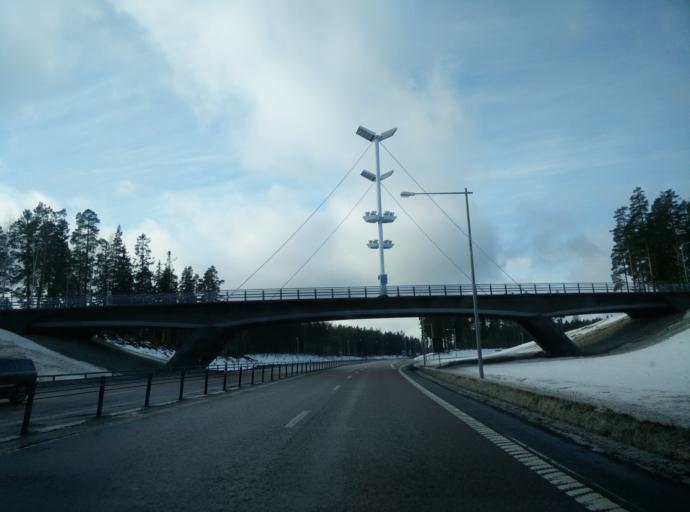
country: SE
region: Gaevleborg
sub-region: Sandvikens Kommun
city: Sandviken
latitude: 60.6237
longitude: 16.7309
